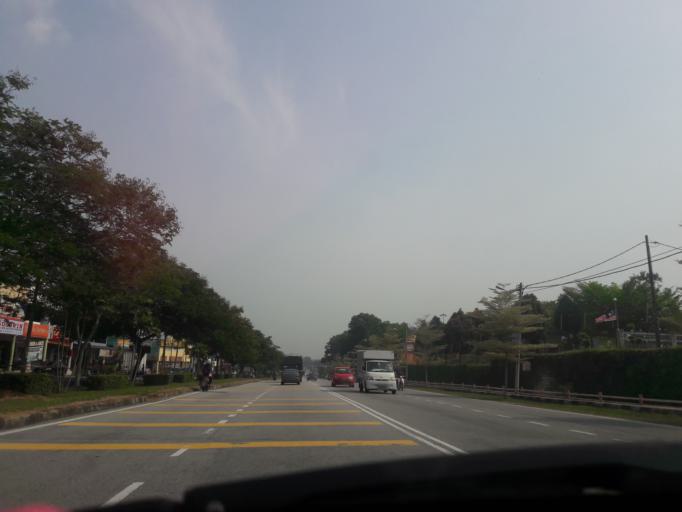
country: MY
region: Kedah
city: Kulim
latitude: 5.3716
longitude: 100.5413
